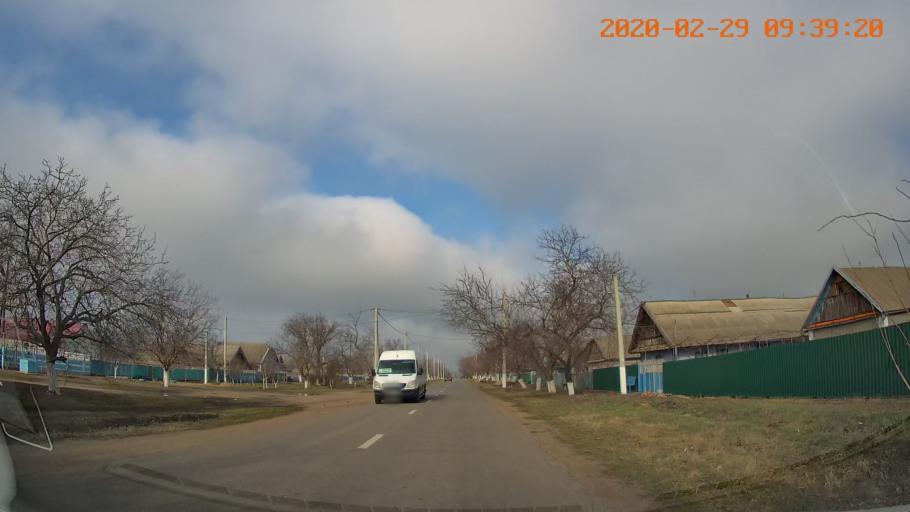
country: MD
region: Telenesti
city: Crasnoe
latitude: 46.6350
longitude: 29.8560
